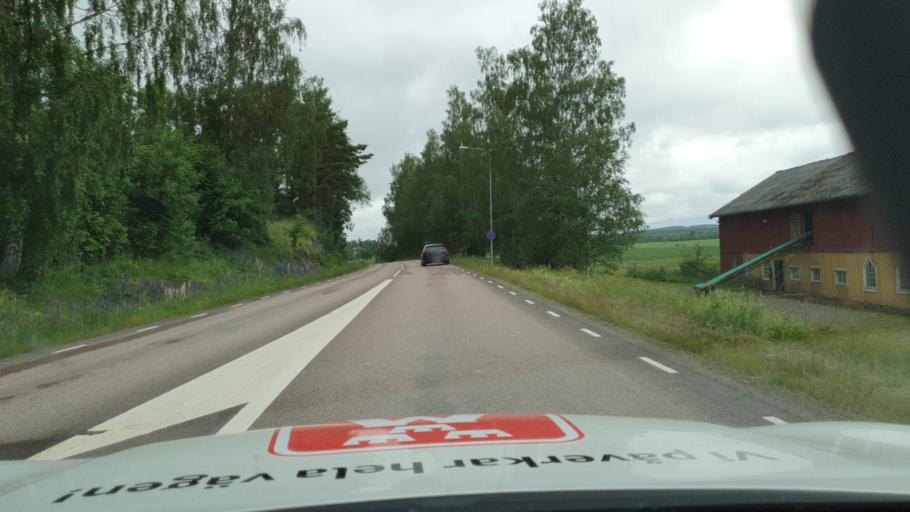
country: SE
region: Vaermland
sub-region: Karlstads Kommun
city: Edsvalla
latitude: 59.4211
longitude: 13.2062
